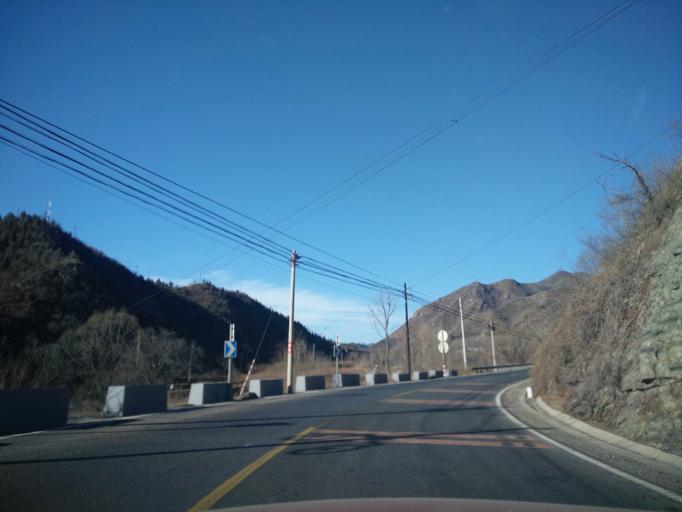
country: CN
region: Beijing
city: Yanchi
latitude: 40.0028
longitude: 115.7857
